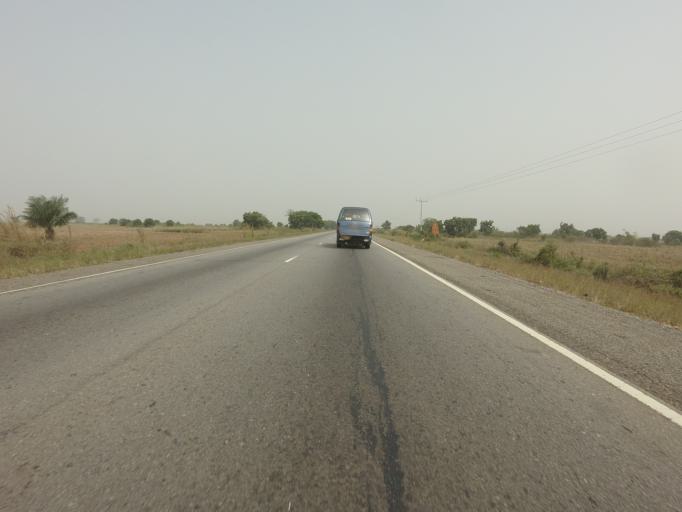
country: GH
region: Volta
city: Anloga
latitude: 5.8858
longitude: 0.4426
